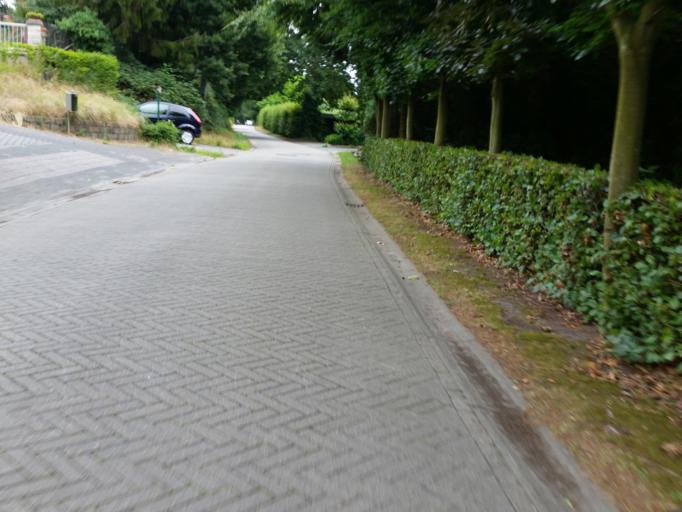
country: BE
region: Flanders
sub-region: Provincie Antwerpen
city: Rumst
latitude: 51.0365
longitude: 4.4316
